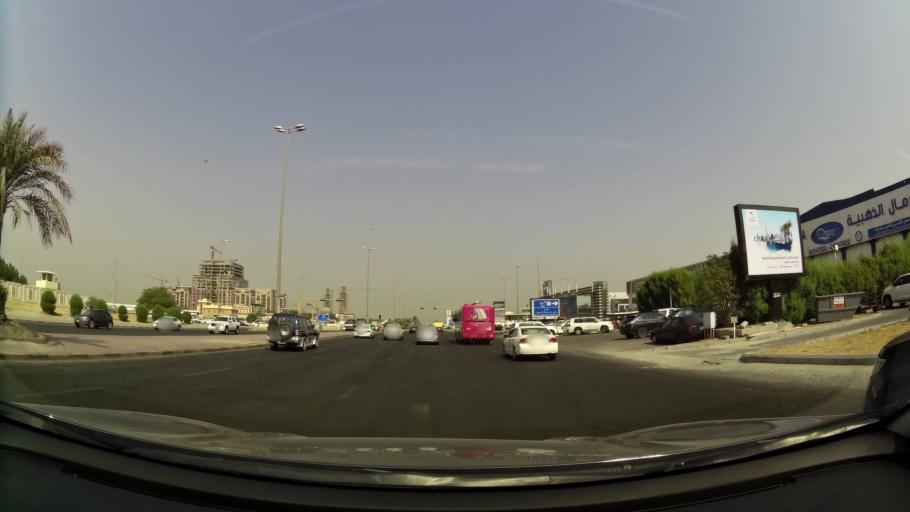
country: KW
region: Al Asimah
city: Ar Rabiyah
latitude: 29.3067
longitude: 47.9270
